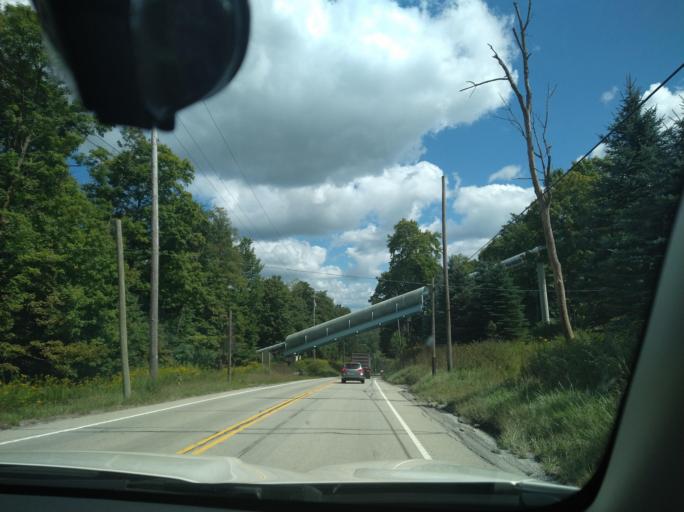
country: US
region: Pennsylvania
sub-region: Westmoreland County
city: Ligonier
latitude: 40.0671
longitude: -79.2526
